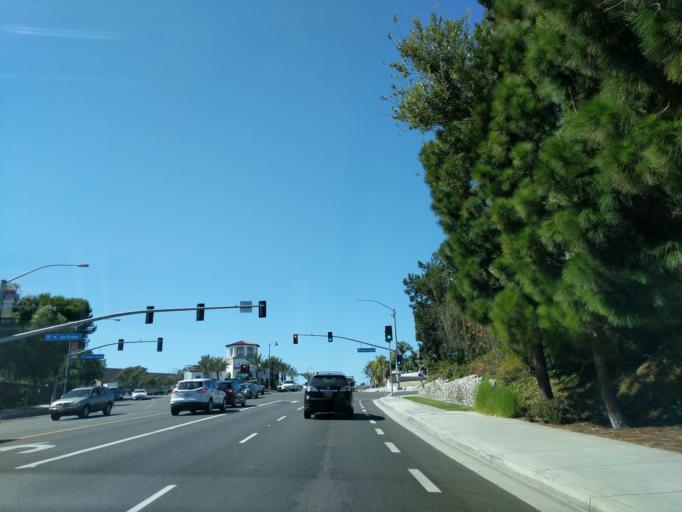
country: US
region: California
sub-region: Orange County
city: Dana Point
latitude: 33.4665
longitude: -117.6932
